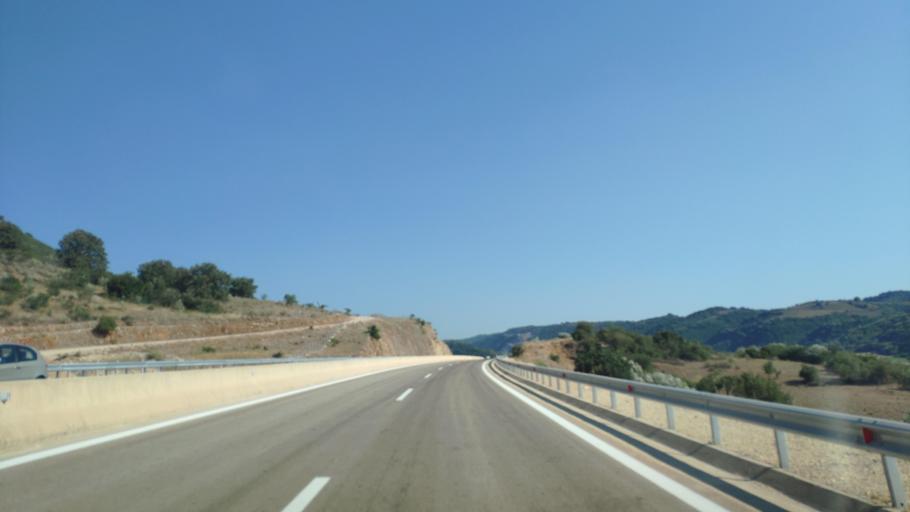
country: GR
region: West Greece
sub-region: Nomos Aitolias kai Akarnanias
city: Katouna
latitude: 38.8075
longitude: 21.1304
